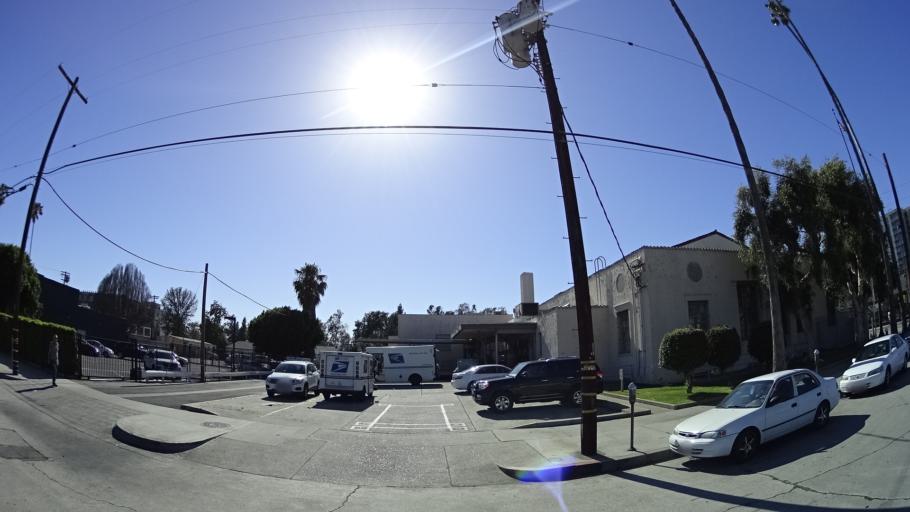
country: US
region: California
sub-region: Los Angeles County
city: North Hollywood
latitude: 34.1675
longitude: -118.3776
